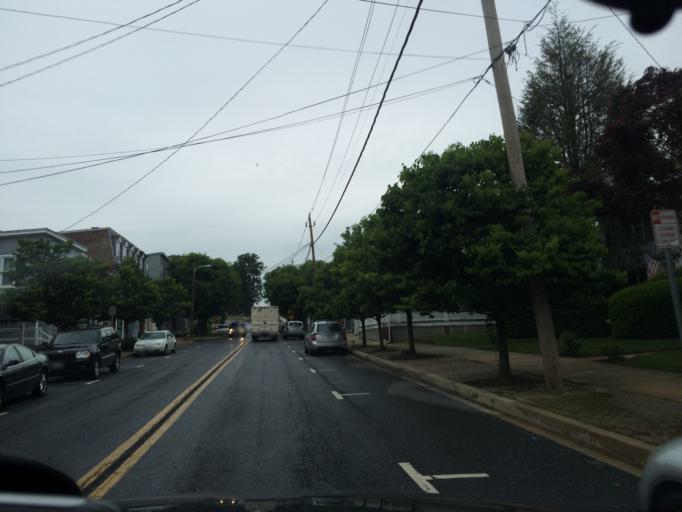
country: US
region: Maryland
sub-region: Carroll County
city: Westminster
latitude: 39.5794
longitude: -77.0002
